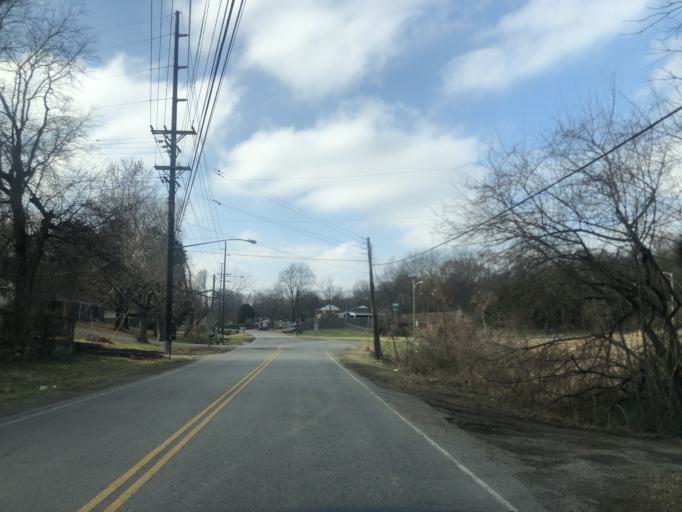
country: US
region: Tennessee
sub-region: Davidson County
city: Oak Hill
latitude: 36.0990
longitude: -86.7167
